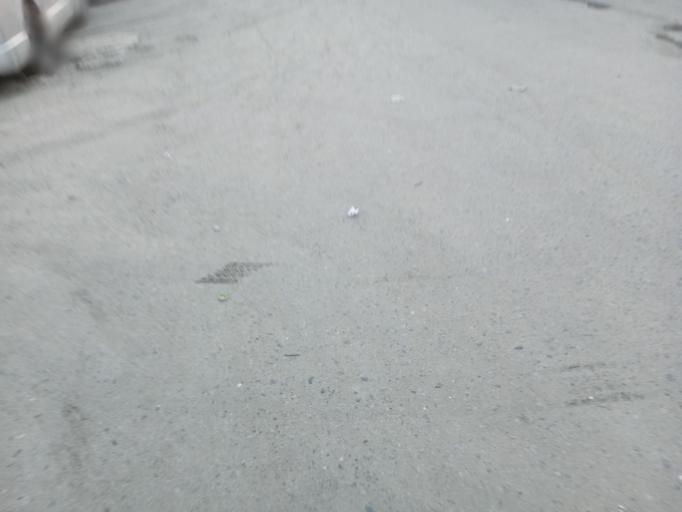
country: ZM
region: Lusaka
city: Lusaka
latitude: -15.4043
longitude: 28.2966
